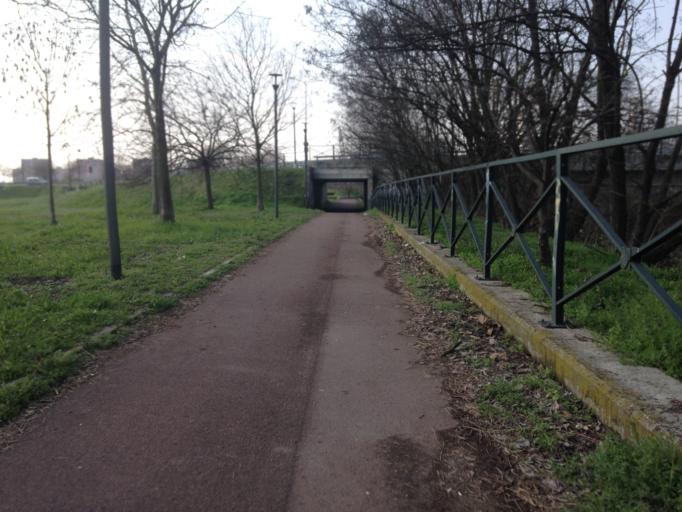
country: IT
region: Lombardy
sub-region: Citta metropolitana di Milano
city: Rozzano
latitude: 45.4248
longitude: 9.1667
